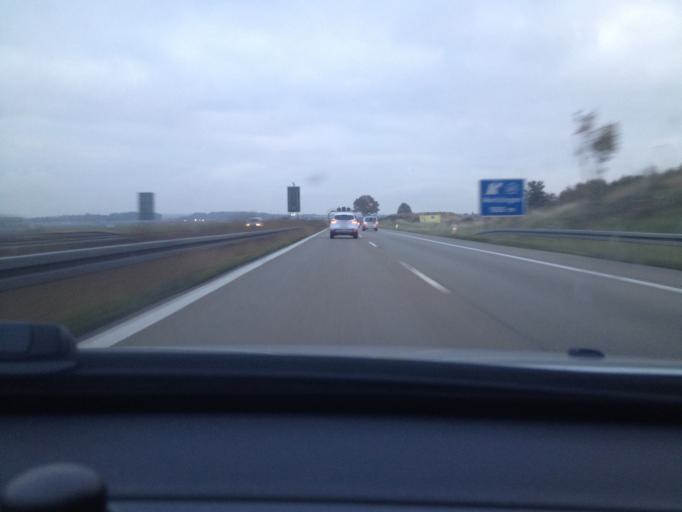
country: DE
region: Baden-Wuerttemberg
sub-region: Tuebingen Region
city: Merklingen
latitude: 48.5218
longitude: 9.7402
